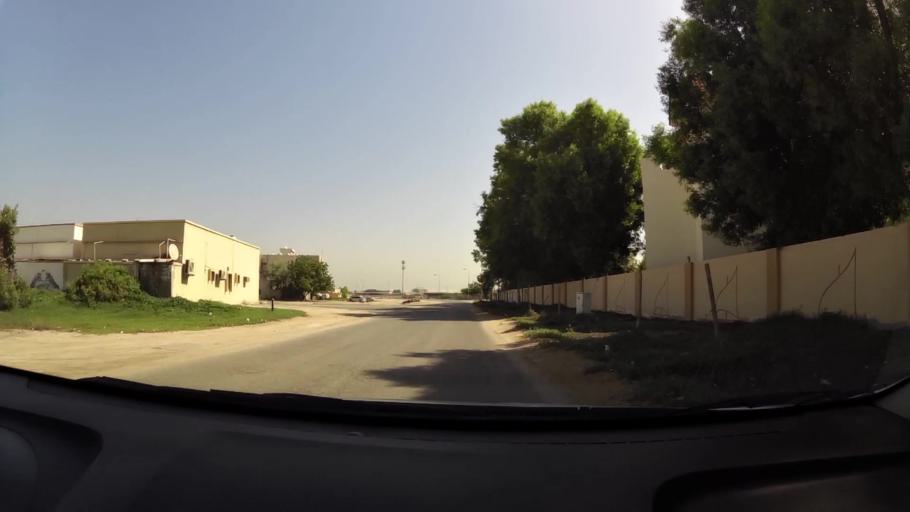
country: AE
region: Umm al Qaywayn
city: Umm al Qaywayn
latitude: 25.5840
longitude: 55.5782
